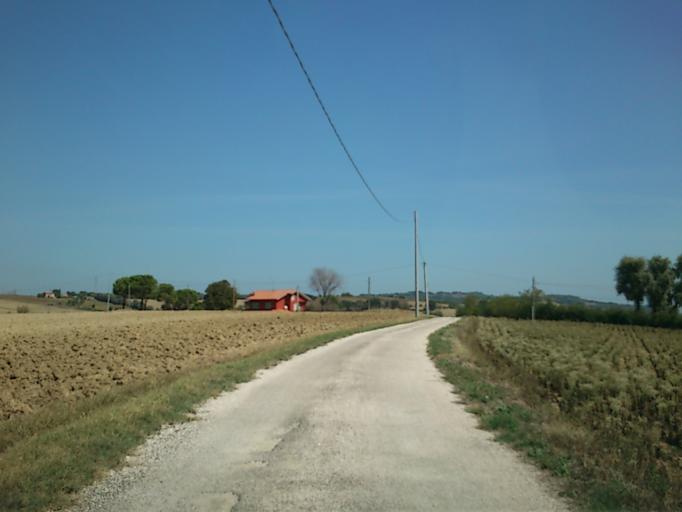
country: IT
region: The Marches
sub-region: Provincia di Pesaro e Urbino
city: Lucrezia
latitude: 43.7846
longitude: 12.9289
